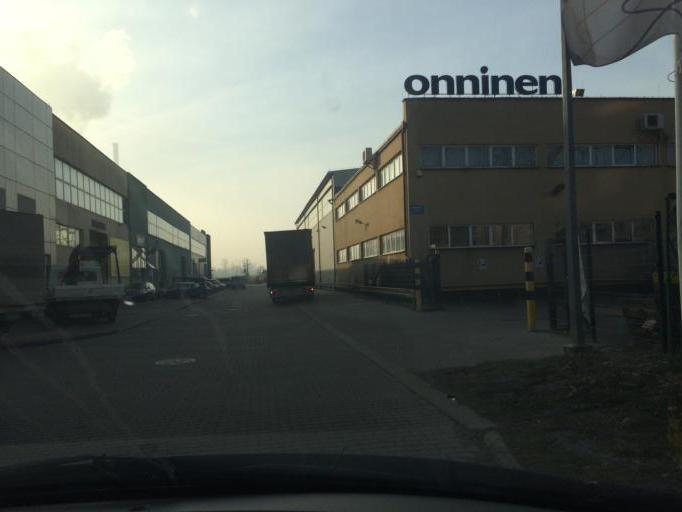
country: PL
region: Lesser Poland Voivodeship
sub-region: Powiat wielicki
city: Czarnochowice
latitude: 50.0619
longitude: 20.0176
